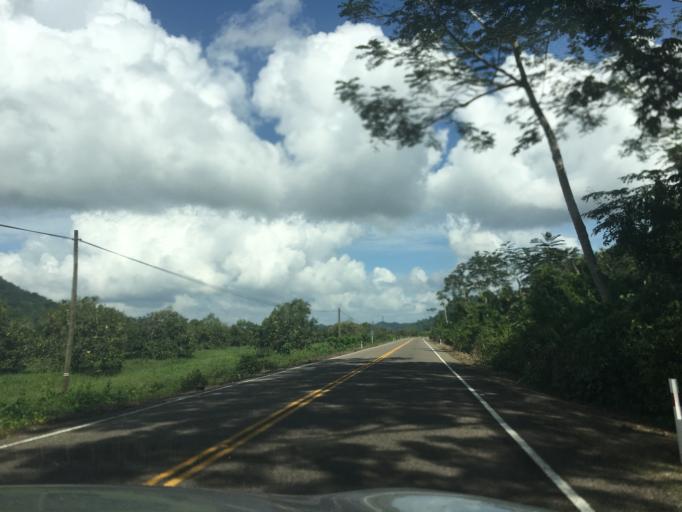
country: BZ
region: Cayo
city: Belmopan
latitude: 17.1487
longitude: -88.6950
